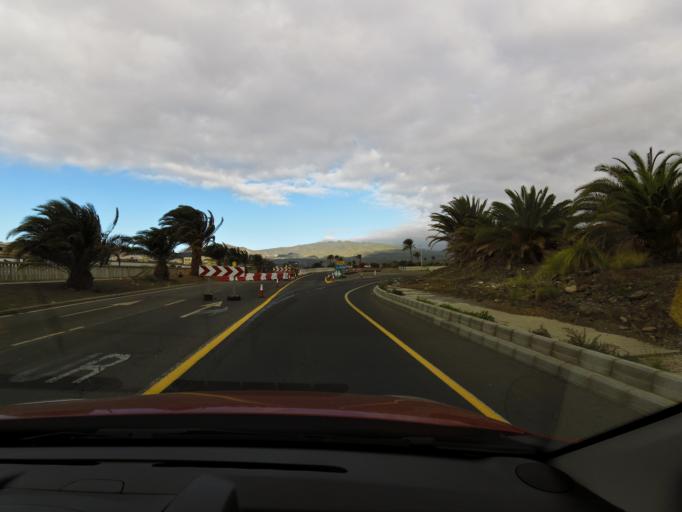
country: ES
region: Canary Islands
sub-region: Provincia de Las Palmas
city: Cruce de Arinaga
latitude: 27.8663
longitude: -15.4231
